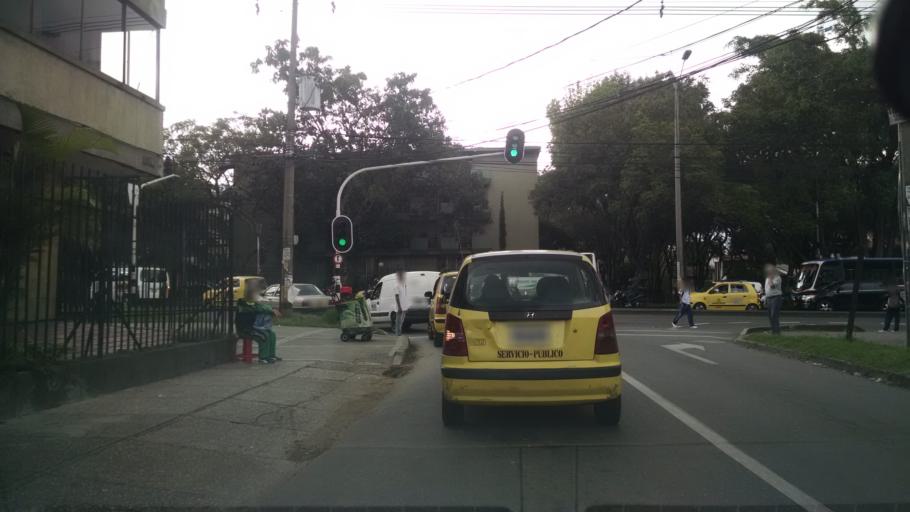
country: CO
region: Antioquia
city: Medellin
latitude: 6.2690
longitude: -75.5957
